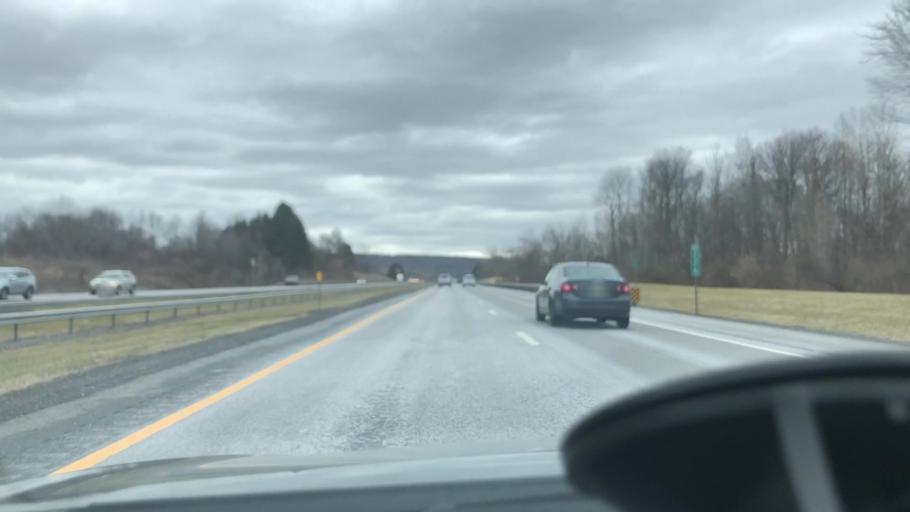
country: US
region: New York
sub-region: Herkimer County
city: Frankfort
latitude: 43.0668
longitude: -75.0871
